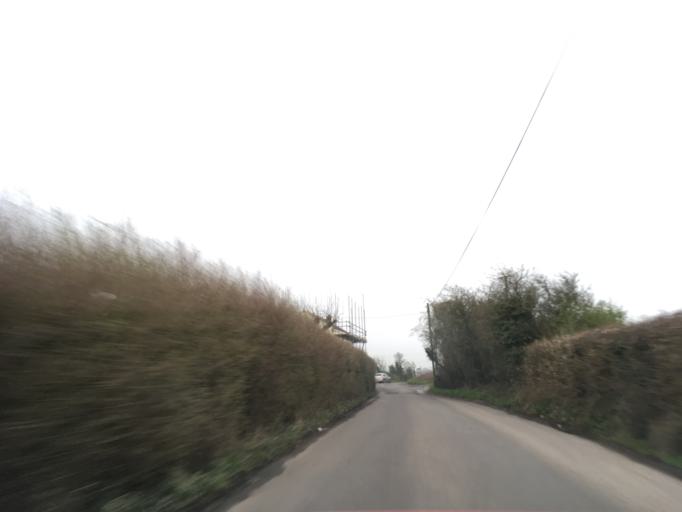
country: GB
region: England
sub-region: South Gloucestershire
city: Winterbourne
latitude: 51.5522
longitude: -2.5151
